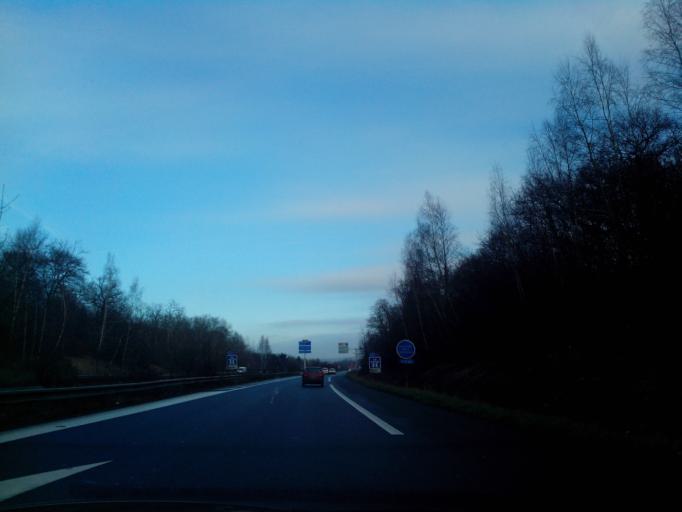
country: FR
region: Ile-de-France
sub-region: Departement du Val-d'Oise
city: L'Isle-Adam
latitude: 49.0960
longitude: 2.2615
